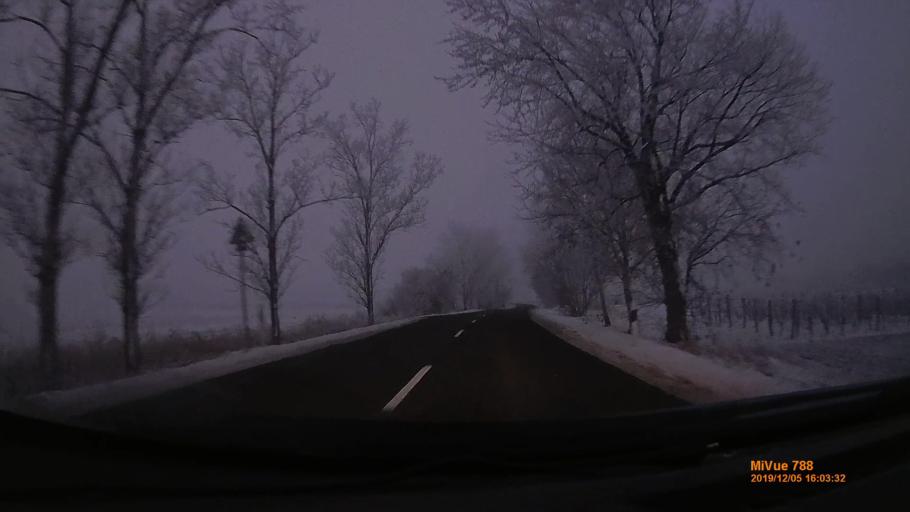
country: HU
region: Borsod-Abauj-Zemplen
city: Tarcal
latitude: 48.1037
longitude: 21.3671
